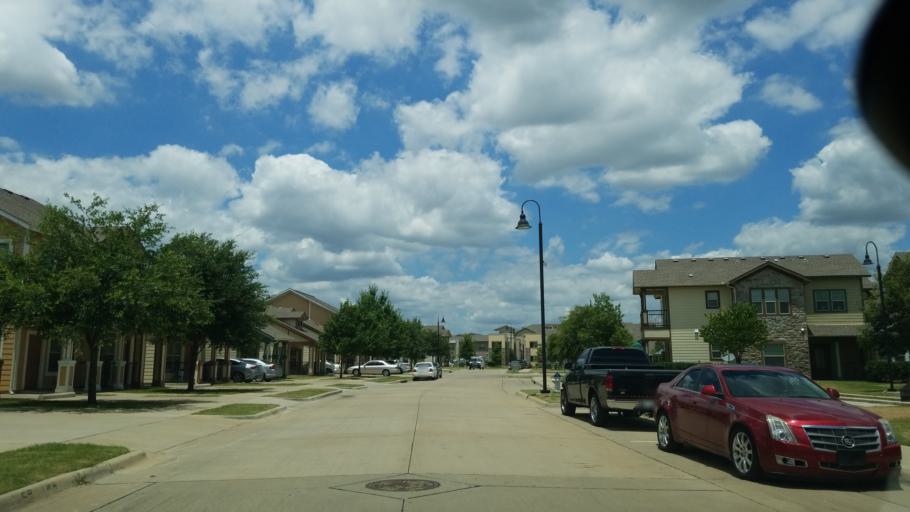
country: US
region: Texas
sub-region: Dallas County
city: Dallas
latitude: 32.7345
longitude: -96.7551
